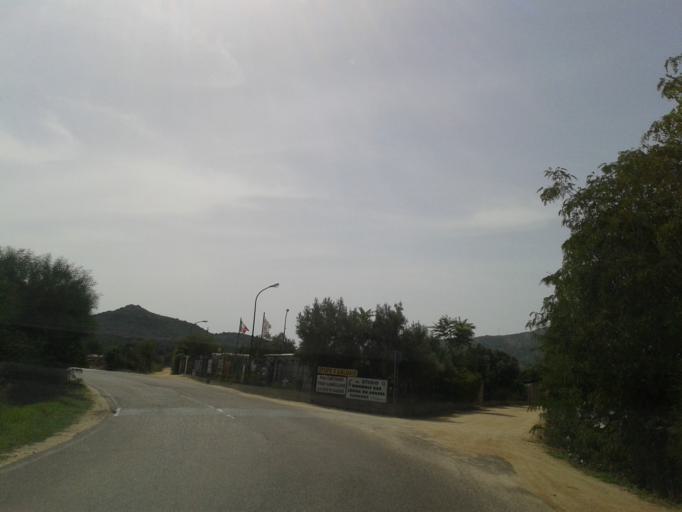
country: IT
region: Sardinia
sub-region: Provincia di Cagliari
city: Villasimius
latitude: 39.1436
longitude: 9.5016
